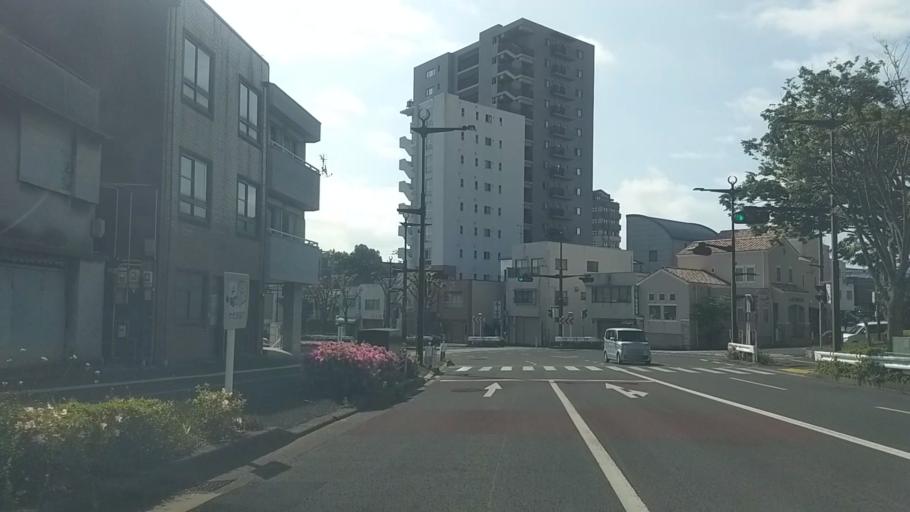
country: JP
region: Shizuoka
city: Hamamatsu
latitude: 34.7111
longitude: 137.7236
